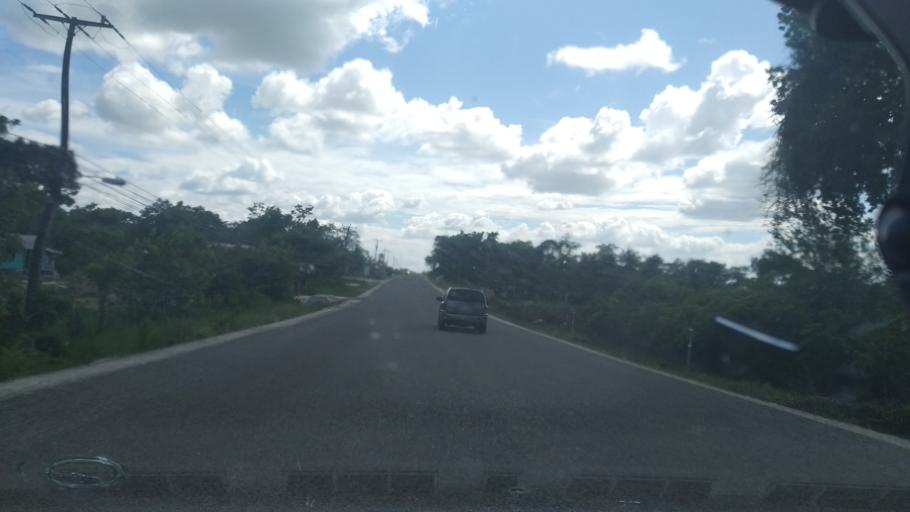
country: BZ
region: Cayo
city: Belmopan
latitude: 17.2529
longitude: -88.8119
